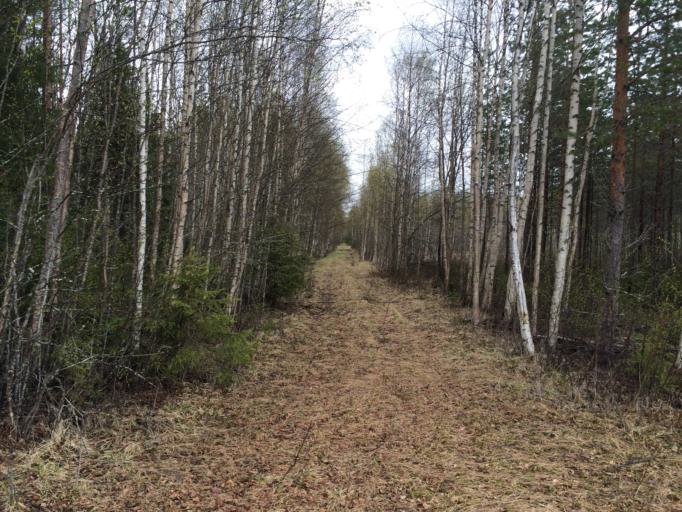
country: SE
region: Norrbotten
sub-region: Bodens Kommun
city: Saevast
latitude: 65.7114
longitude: 21.8300
